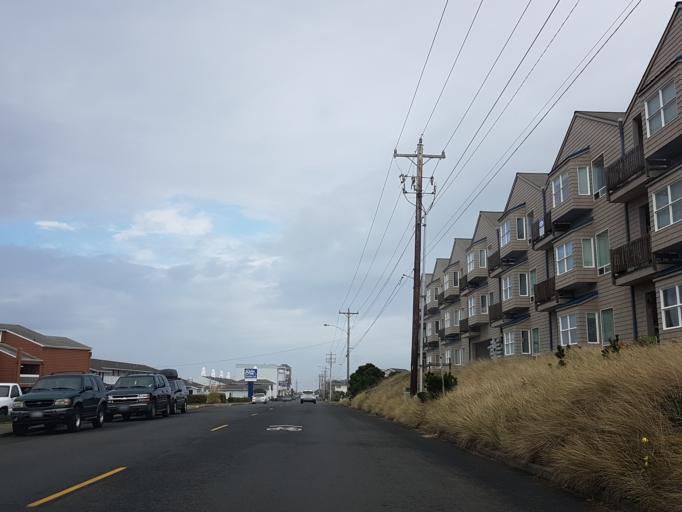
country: US
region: Oregon
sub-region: Lincoln County
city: Newport
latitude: 44.6303
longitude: -124.0634
